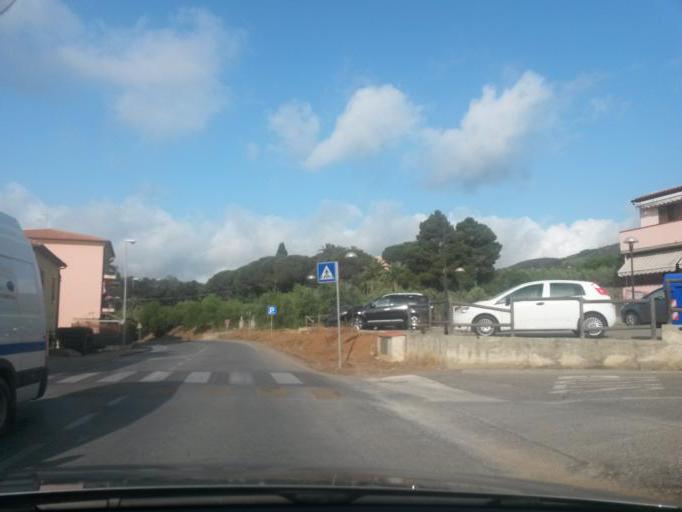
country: IT
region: Tuscany
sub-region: Provincia di Livorno
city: Porto Azzurro
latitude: 42.7702
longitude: 10.3979
